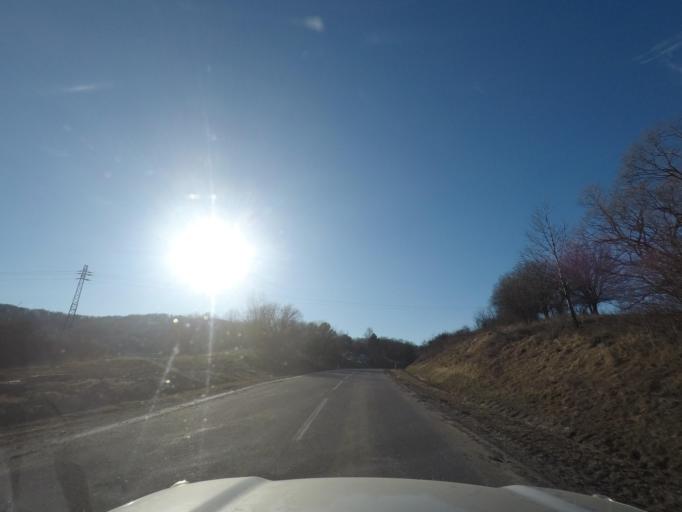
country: SK
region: Presovsky
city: Medzilaborce
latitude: 49.2352
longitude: 21.9492
